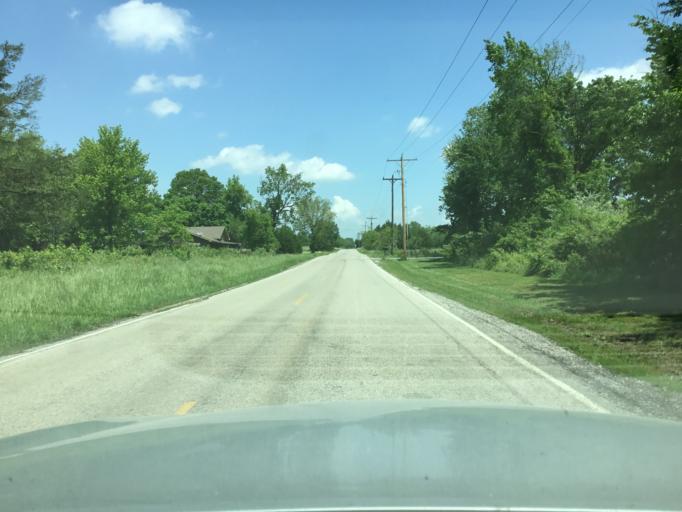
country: US
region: Kansas
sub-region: Labette County
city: Parsons
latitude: 37.3430
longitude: -95.3038
